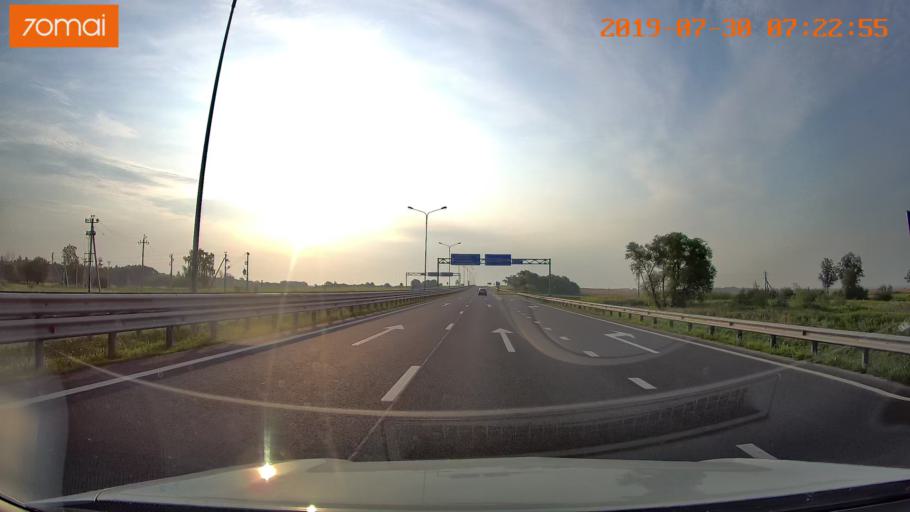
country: RU
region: Kaliningrad
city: Bol'shoe Isakovo
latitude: 54.6920
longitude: 20.7695
